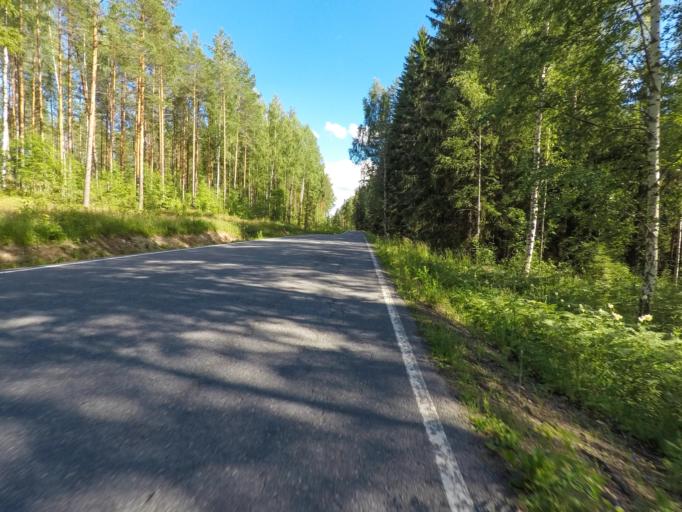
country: FI
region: South Karelia
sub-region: Lappeenranta
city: Taipalsaari
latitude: 61.1739
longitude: 28.0157
